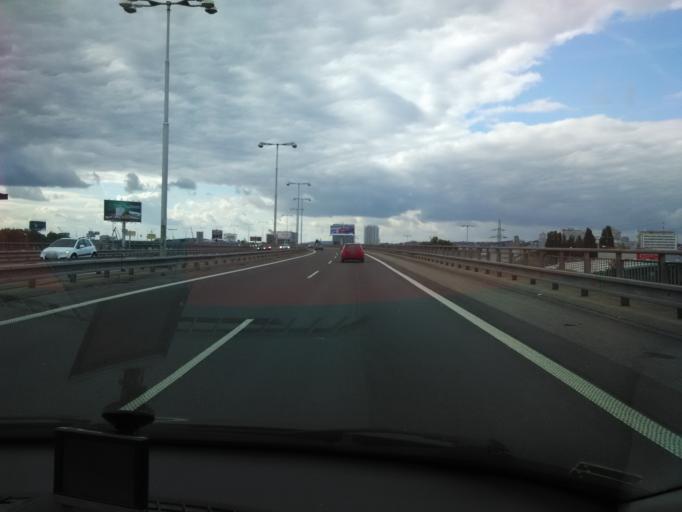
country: SK
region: Bratislavsky
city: Bratislava
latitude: 48.1421
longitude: 17.1544
